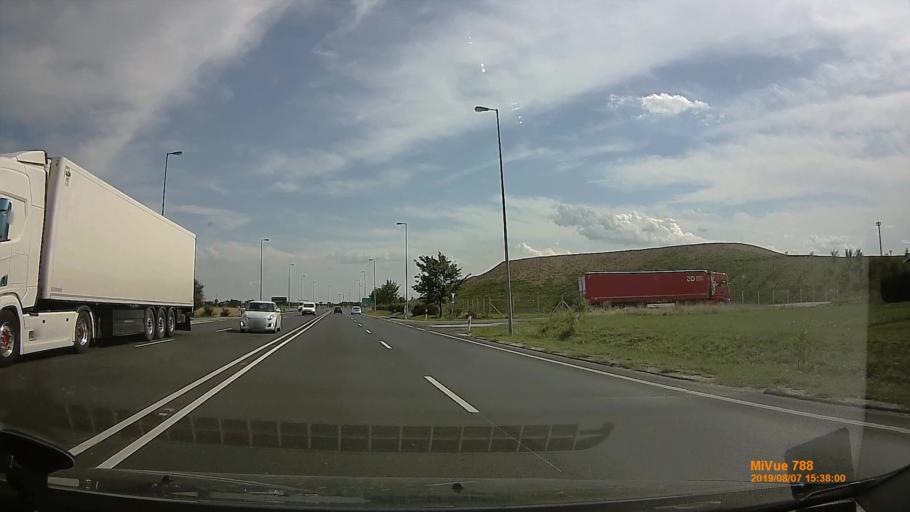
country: HU
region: Vas
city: Szombathely
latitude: 47.2361
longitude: 16.6563
